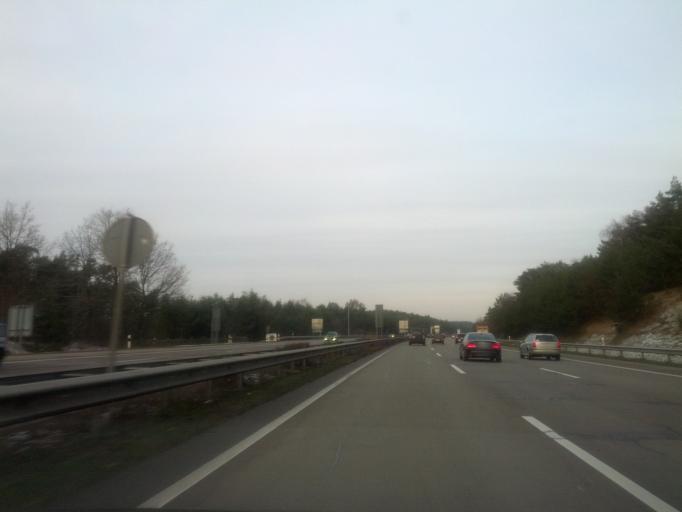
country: DE
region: Lower Saxony
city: Soltau
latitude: 53.0109
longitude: 9.9304
